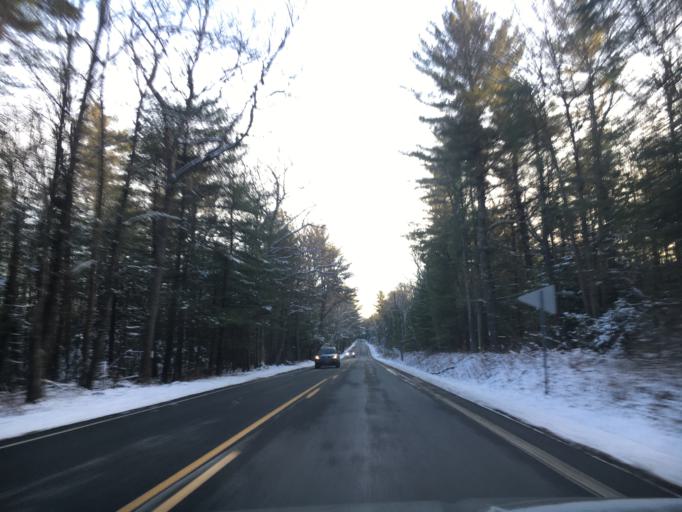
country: US
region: Pennsylvania
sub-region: Pike County
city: Hemlock Farms
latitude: 41.3451
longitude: -75.1316
